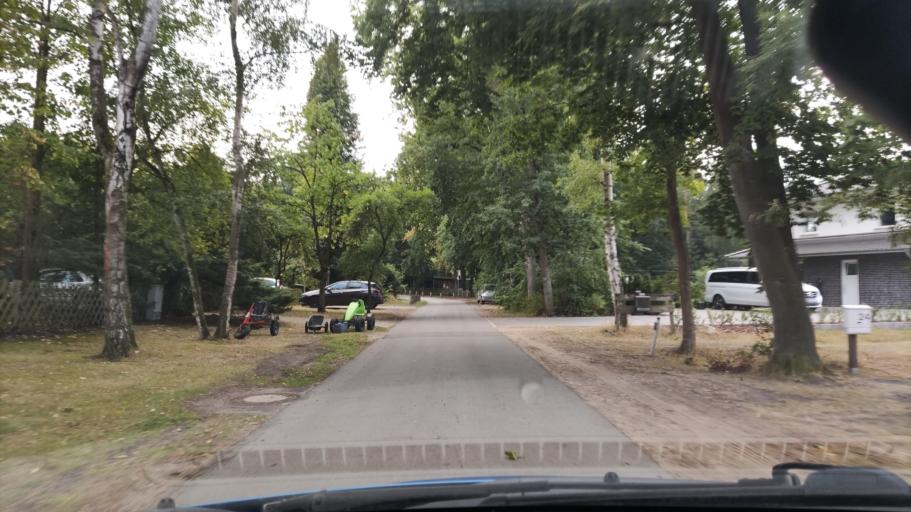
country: DE
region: Lower Saxony
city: Barum
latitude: 53.3462
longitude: 10.4100
